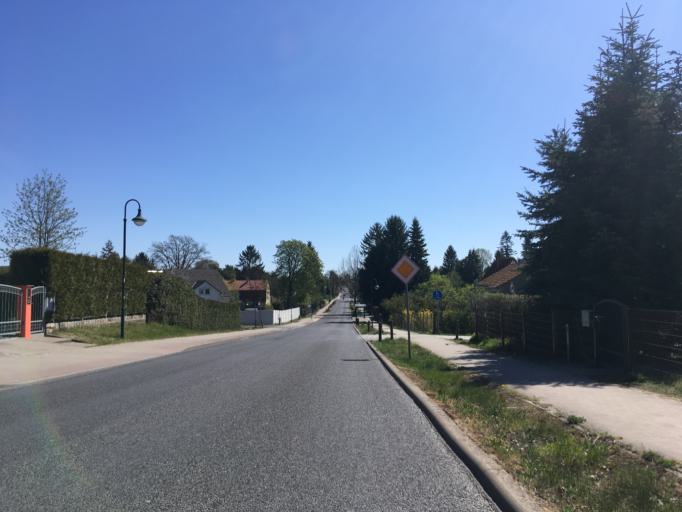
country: DE
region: Brandenburg
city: Bernau bei Berlin
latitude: 52.6475
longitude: 13.5501
